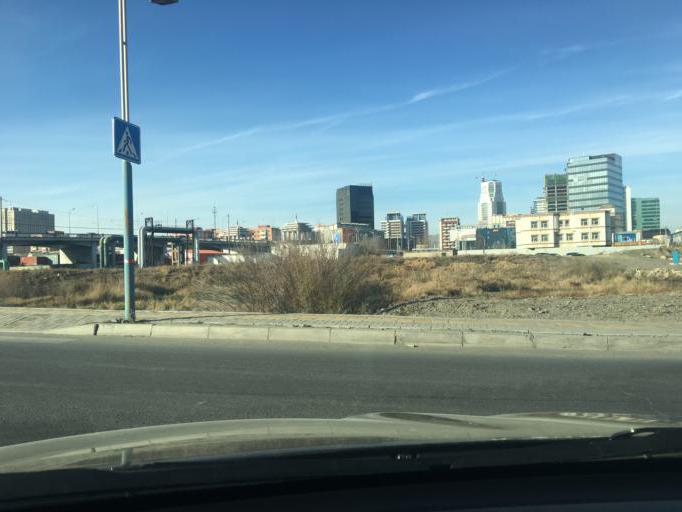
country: MN
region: Ulaanbaatar
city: Ulaanbaatar
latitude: 47.9068
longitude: 106.9145
